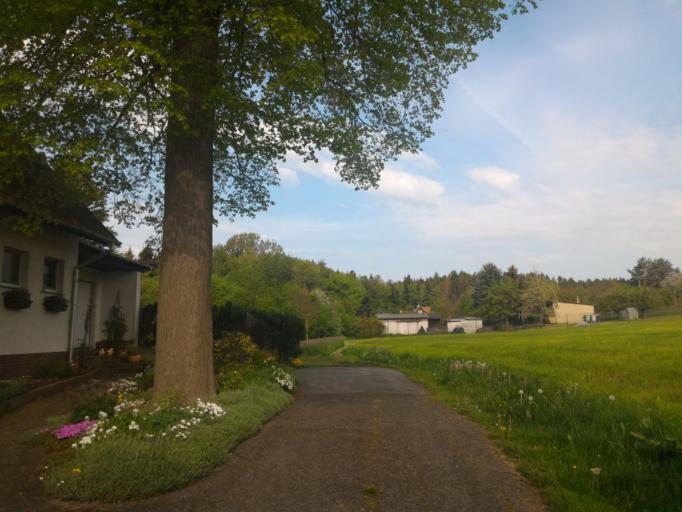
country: DE
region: Saxony
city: Leutersdorf
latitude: 50.9552
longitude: 14.6264
